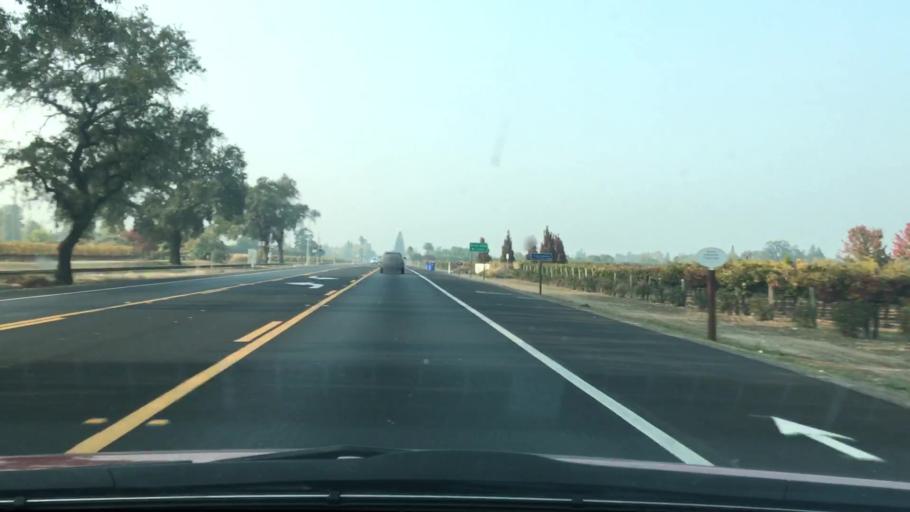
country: US
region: California
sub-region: Napa County
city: Yountville
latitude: 38.4490
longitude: -122.4137
